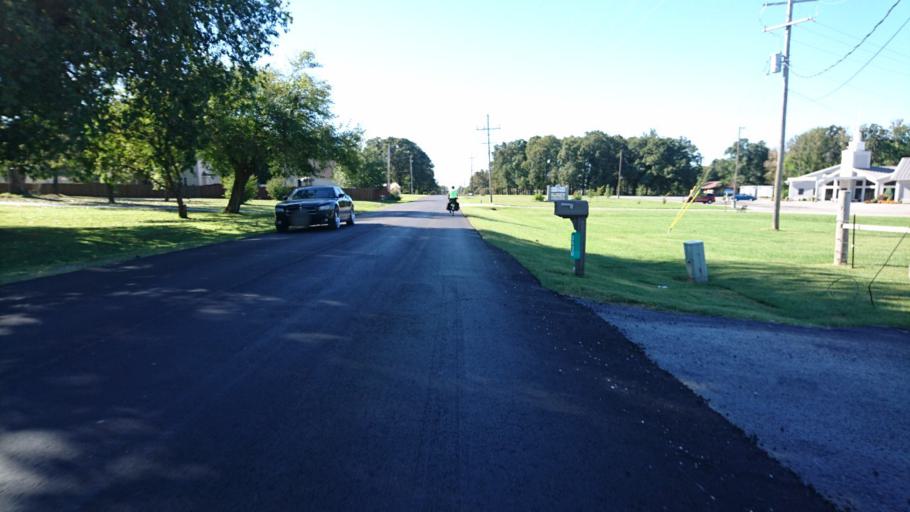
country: US
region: Missouri
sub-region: Jasper County
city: Joplin
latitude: 37.1183
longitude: -94.4938
